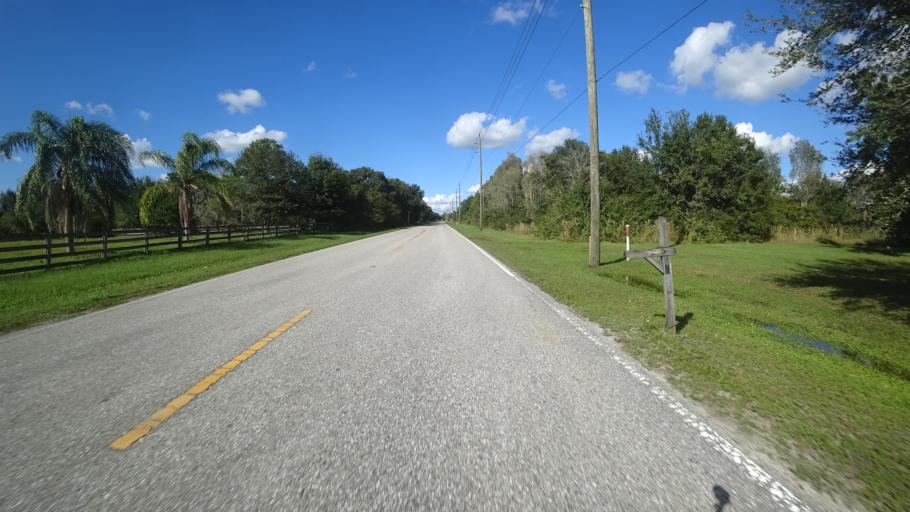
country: US
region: Florida
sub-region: Sarasota County
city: Lake Sarasota
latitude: 27.3801
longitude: -82.2683
